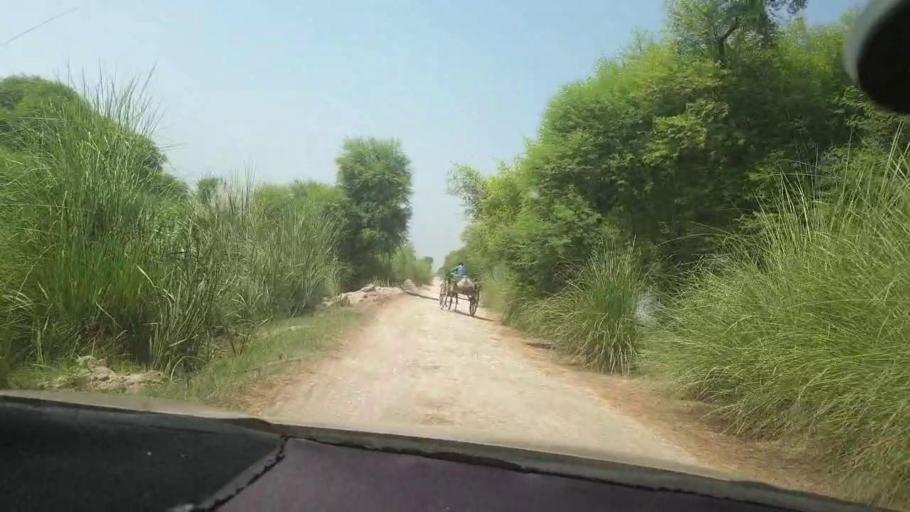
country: PK
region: Sindh
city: Shahdadkot
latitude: 27.7167
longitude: 67.9412
